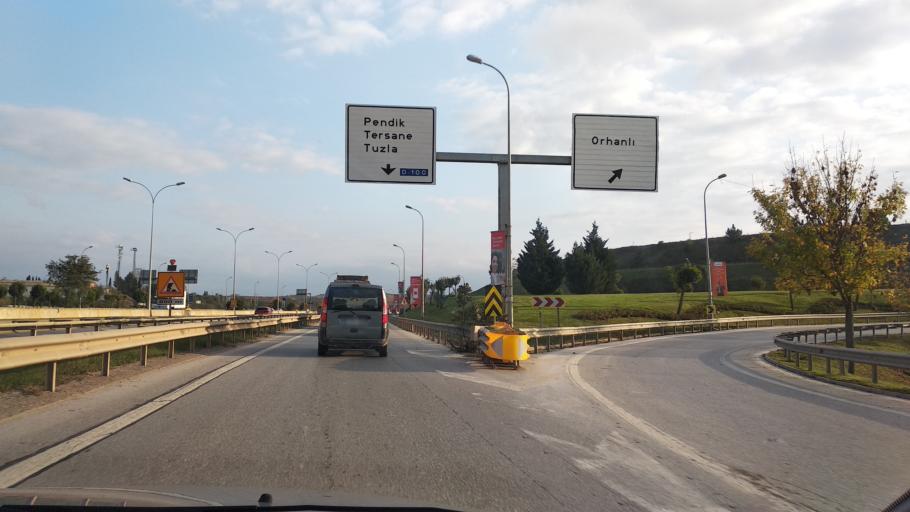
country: TR
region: Istanbul
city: Pendik
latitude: 40.9140
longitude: 29.3248
